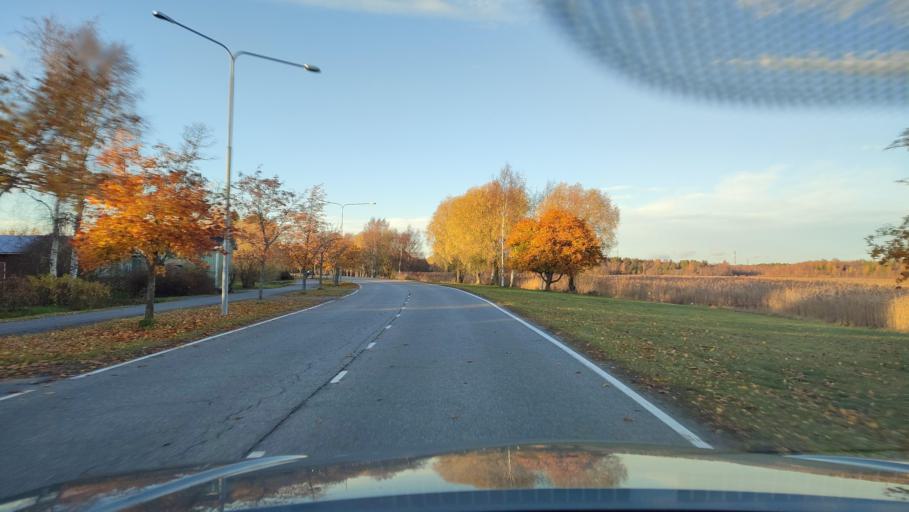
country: FI
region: Ostrobothnia
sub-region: Sydosterbotten
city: Kristinestad
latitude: 62.2789
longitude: 21.3807
